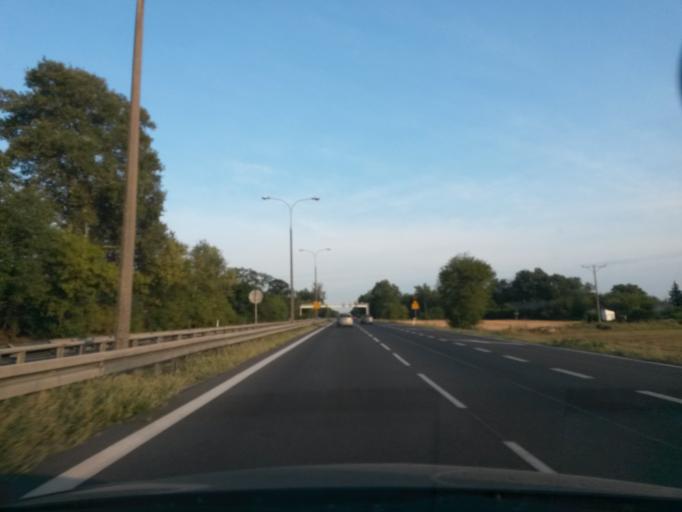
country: PL
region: Masovian Voivodeship
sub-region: Powiat nowodworski
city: Nowy Dwor Mazowiecki
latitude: 52.4081
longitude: 20.7011
